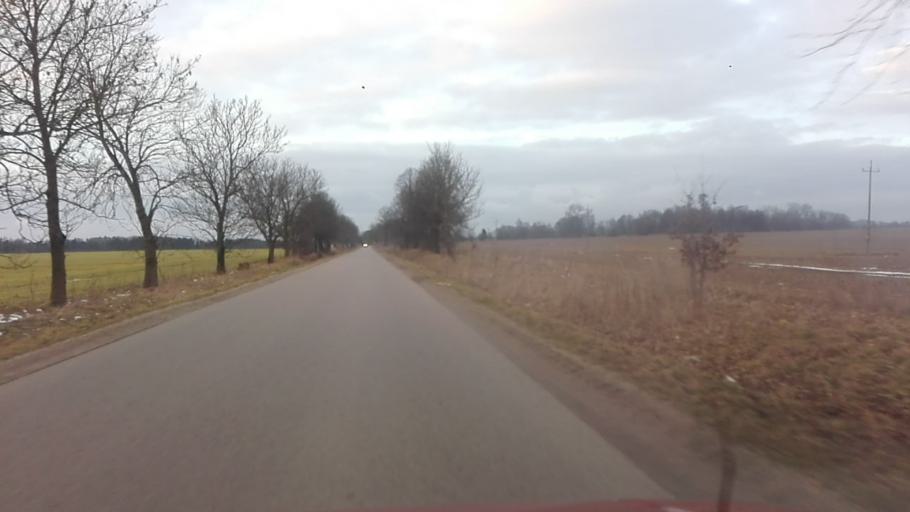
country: PL
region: West Pomeranian Voivodeship
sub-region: Powiat swidwinski
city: Rabino
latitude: 53.7898
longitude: 15.9041
